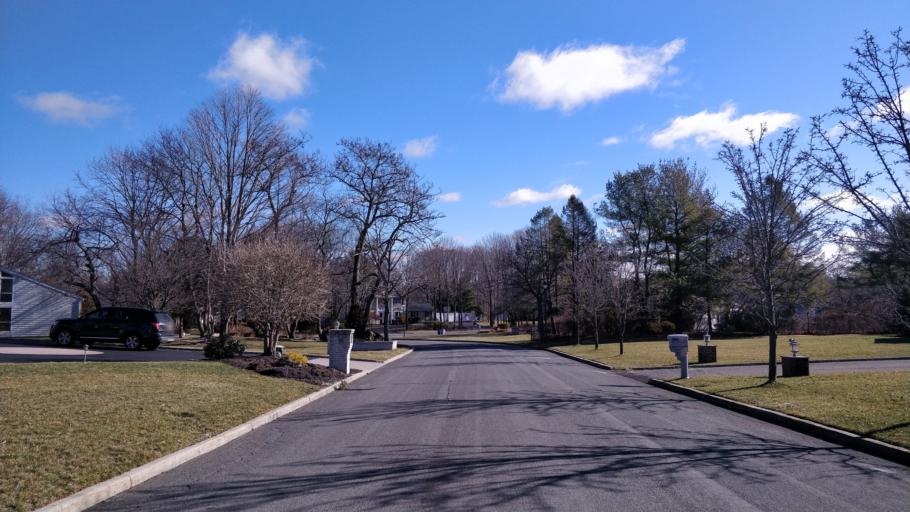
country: US
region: New York
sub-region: Suffolk County
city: Saint James
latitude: 40.8845
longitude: -73.1402
